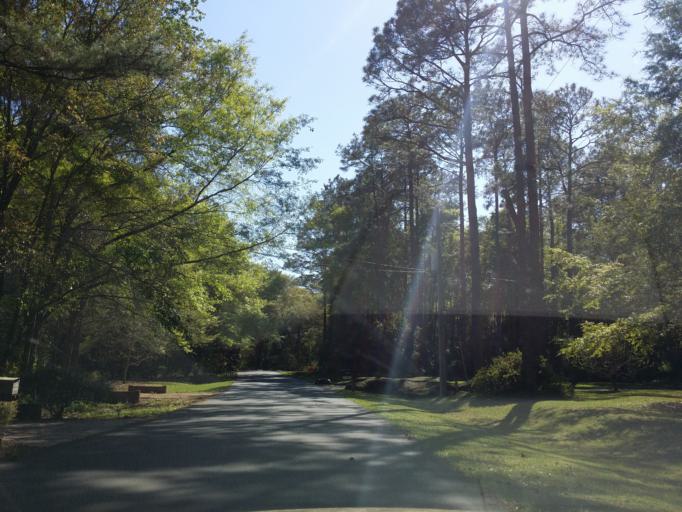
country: US
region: Florida
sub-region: Leon County
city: Tallahassee
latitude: 30.4876
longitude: -84.1889
